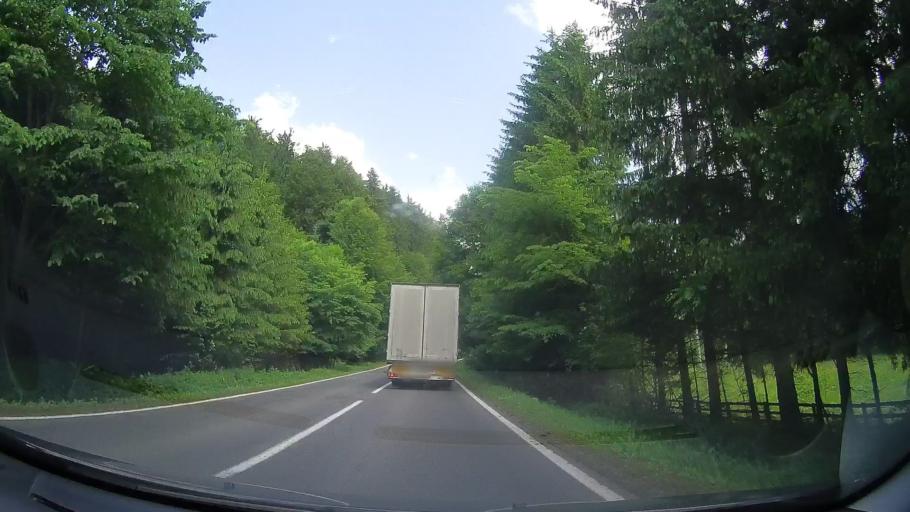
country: RO
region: Prahova
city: Maneciu
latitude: 45.3718
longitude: 25.9302
